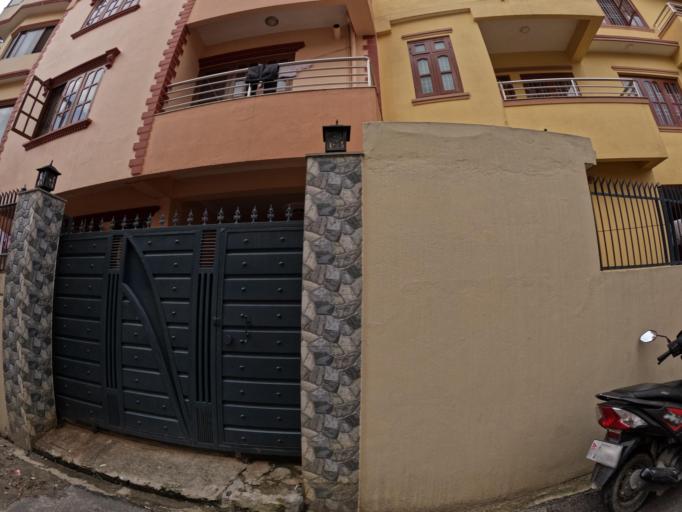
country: NP
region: Central Region
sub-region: Bagmati Zone
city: Kathmandu
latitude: 27.7417
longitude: 85.3180
